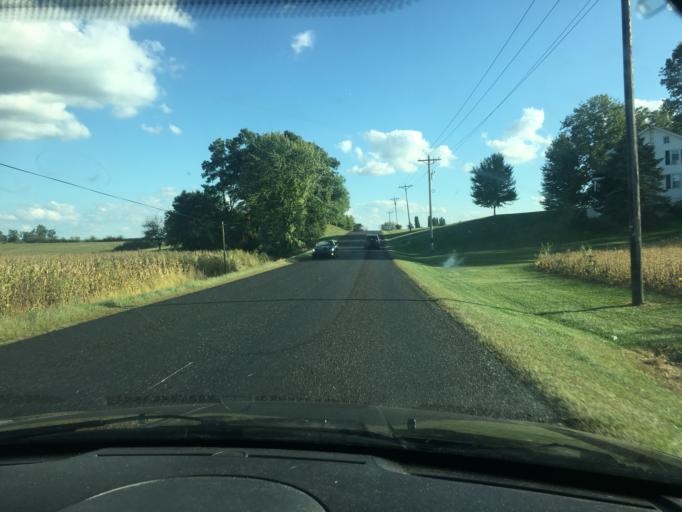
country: US
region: Ohio
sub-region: Logan County
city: West Liberty
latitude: 40.2926
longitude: -83.7298
